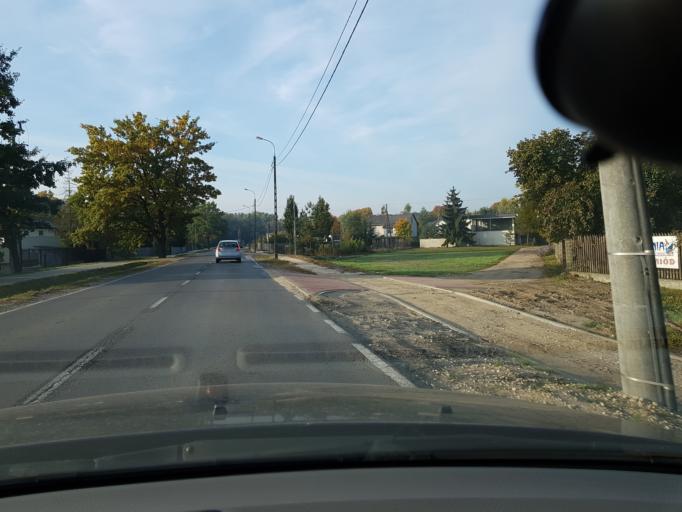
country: PL
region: Masovian Voivodeship
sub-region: Powiat otwocki
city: Jozefow
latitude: 52.1791
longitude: 21.2978
